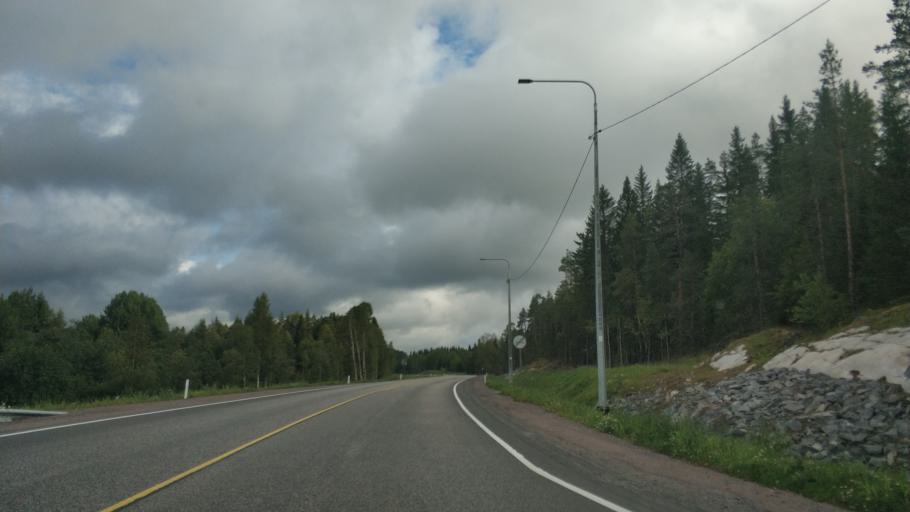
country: RU
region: Republic of Karelia
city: Khelyulya
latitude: 61.8028
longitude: 30.6167
